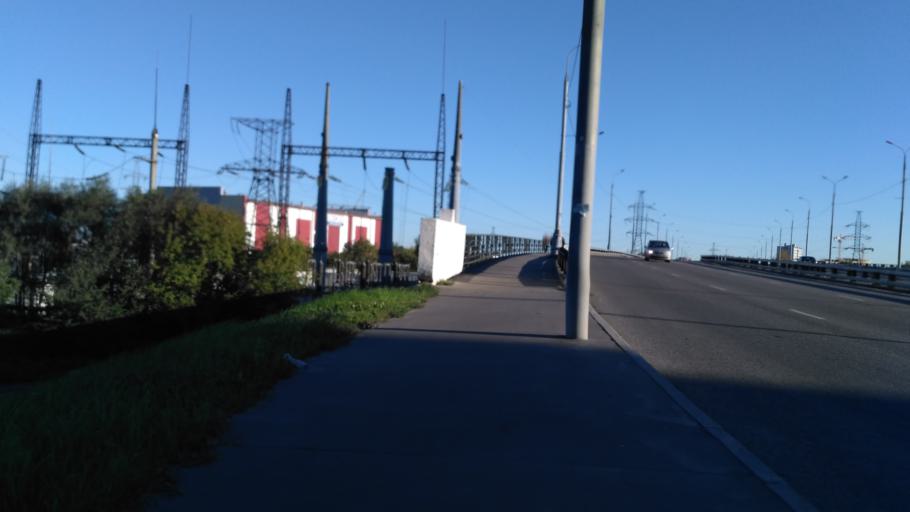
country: RU
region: Moscow
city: Novovladykino
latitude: 55.8311
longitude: 37.5771
